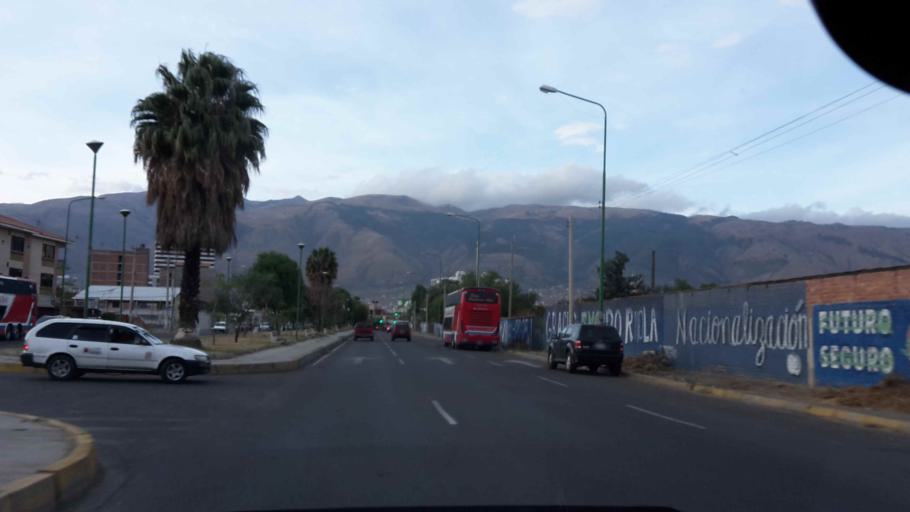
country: BO
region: Cochabamba
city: Cochabamba
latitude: -17.3899
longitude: -66.1830
